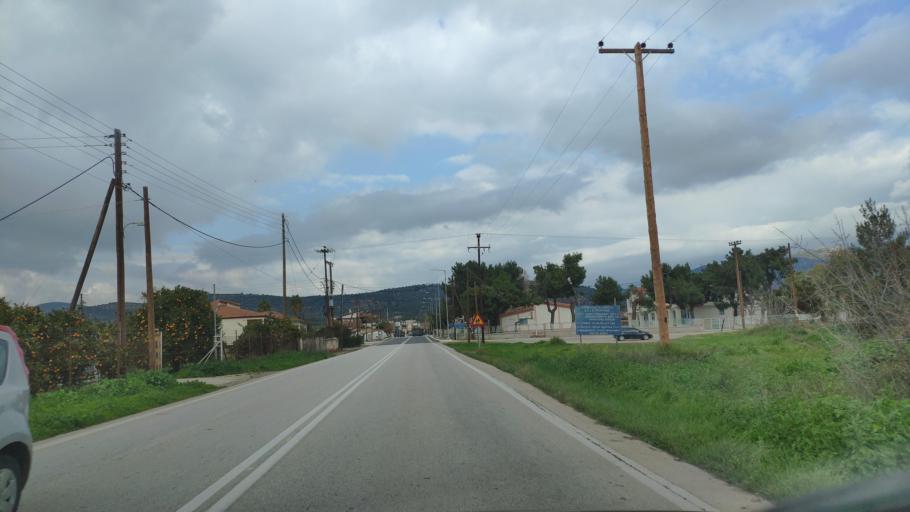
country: GR
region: Peloponnese
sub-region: Nomos Argolidos
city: Koutsopodi
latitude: 37.7174
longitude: 22.7250
